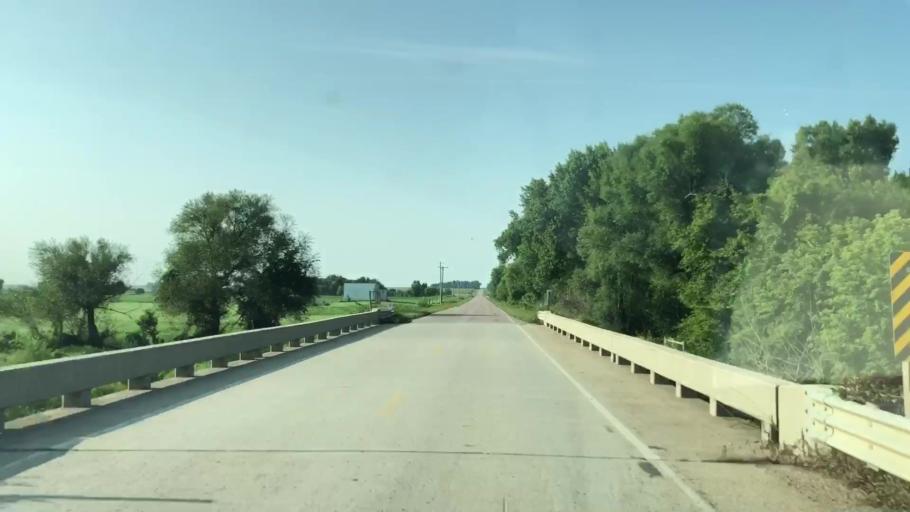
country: US
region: Iowa
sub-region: Lyon County
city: George
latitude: 43.2531
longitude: -96.0003
